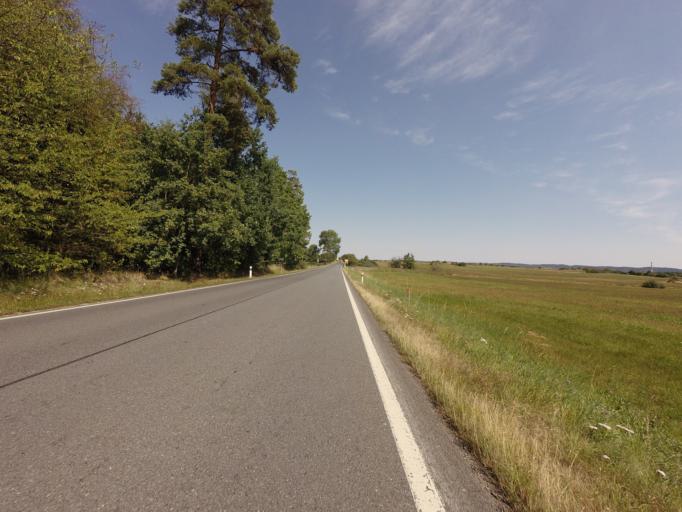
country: CZ
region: Jihocesky
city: Milevsko
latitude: 49.4277
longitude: 14.3593
